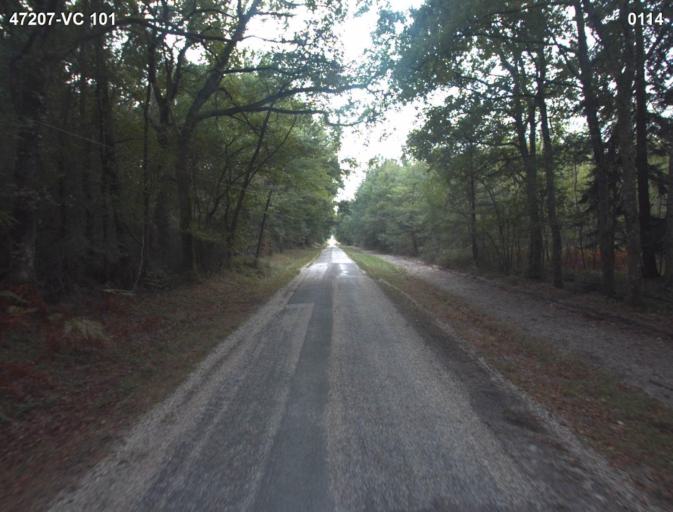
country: FR
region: Aquitaine
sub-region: Departement du Lot-et-Garonne
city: Barbaste
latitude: 44.1911
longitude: 0.2006
